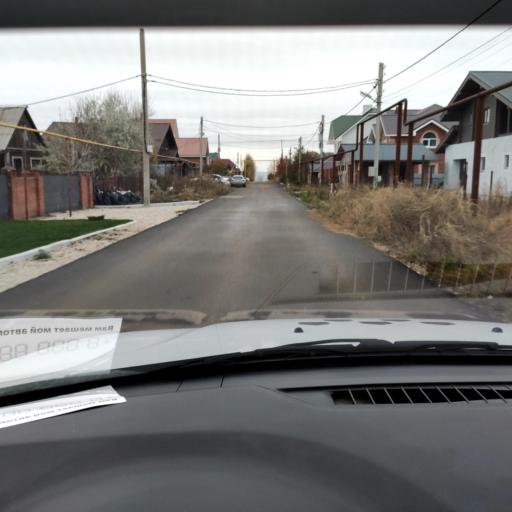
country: RU
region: Samara
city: Podstepki
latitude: 53.5138
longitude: 49.2078
